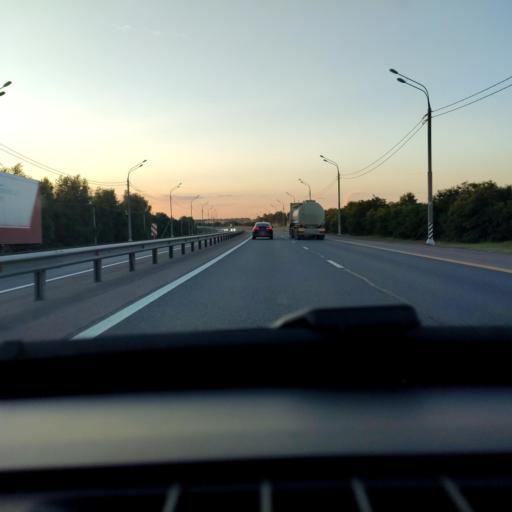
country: RU
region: Lipetsk
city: Khlevnoye
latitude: 52.1741
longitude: 39.1940
